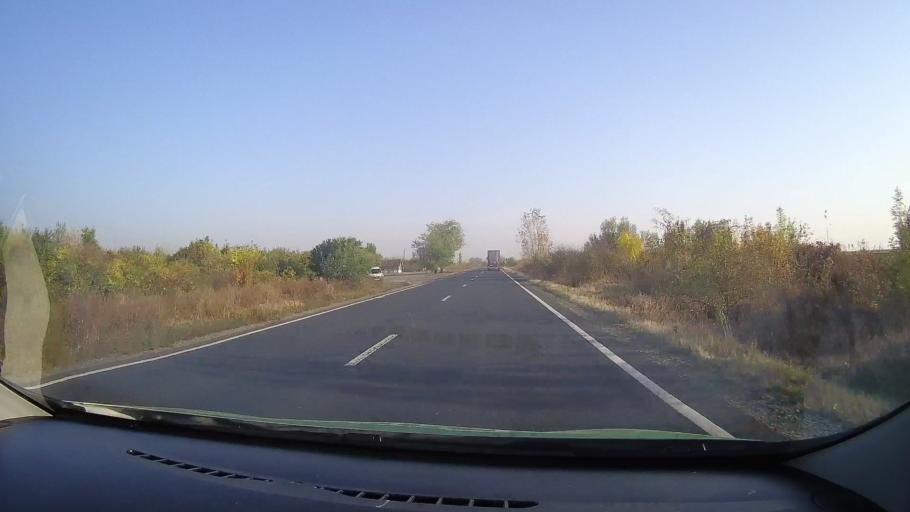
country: RO
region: Arad
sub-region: Comuna Simand
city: Simand
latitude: 46.3986
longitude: 21.4420
